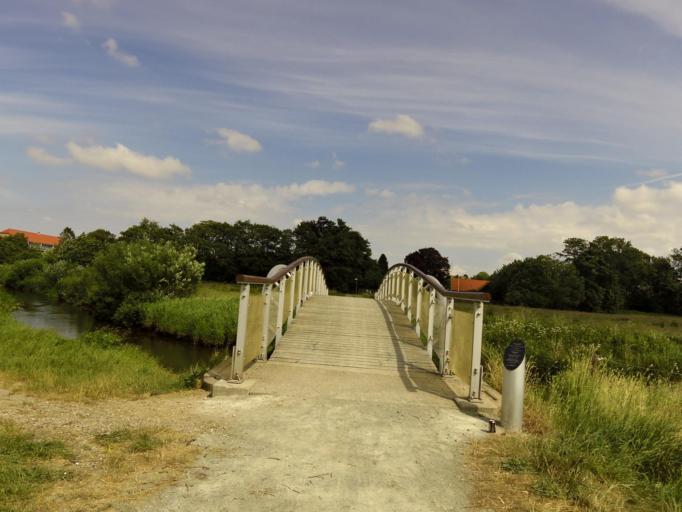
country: DK
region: South Denmark
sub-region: Tonder Kommune
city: Logumkloster
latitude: 55.0597
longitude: 8.9453
